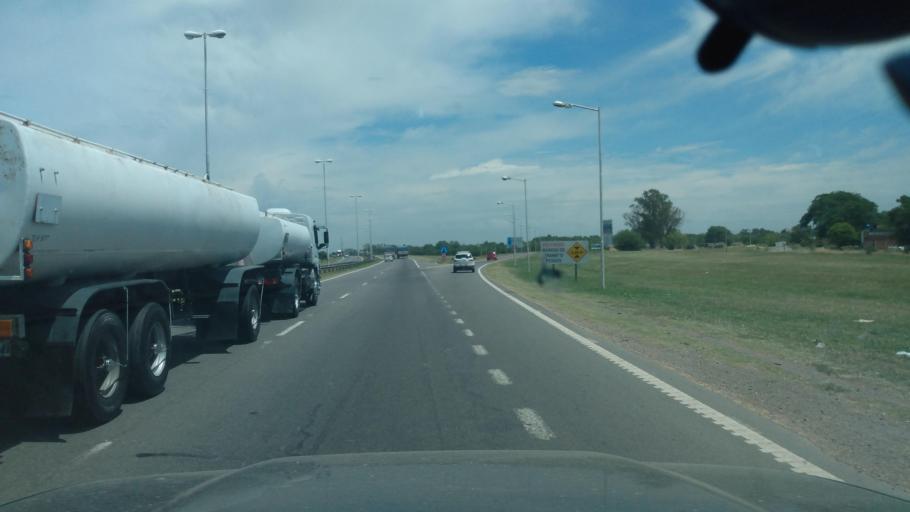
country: AR
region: Buenos Aires
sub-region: Partido de Lujan
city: Lujan
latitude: -34.5510
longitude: -59.1098
